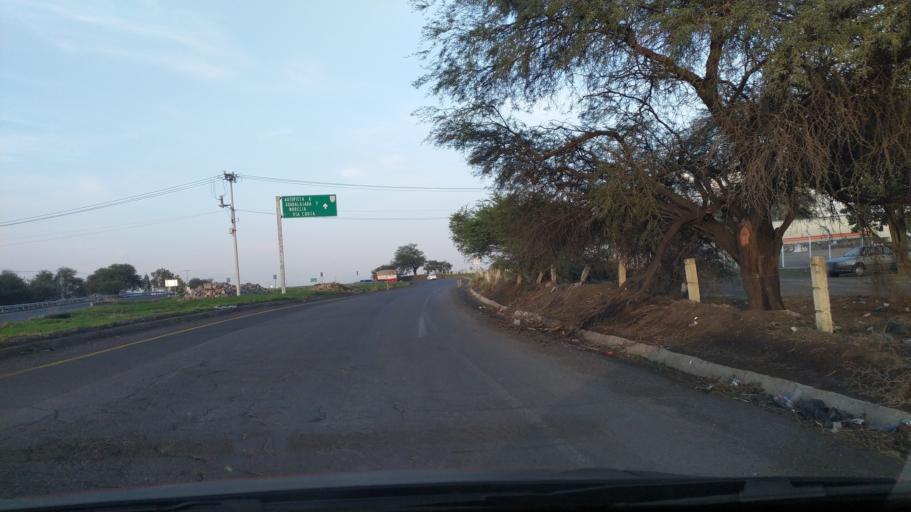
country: MX
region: Michoacan
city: Vistahermosa de Negrete
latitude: 20.2684
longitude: -102.4479
